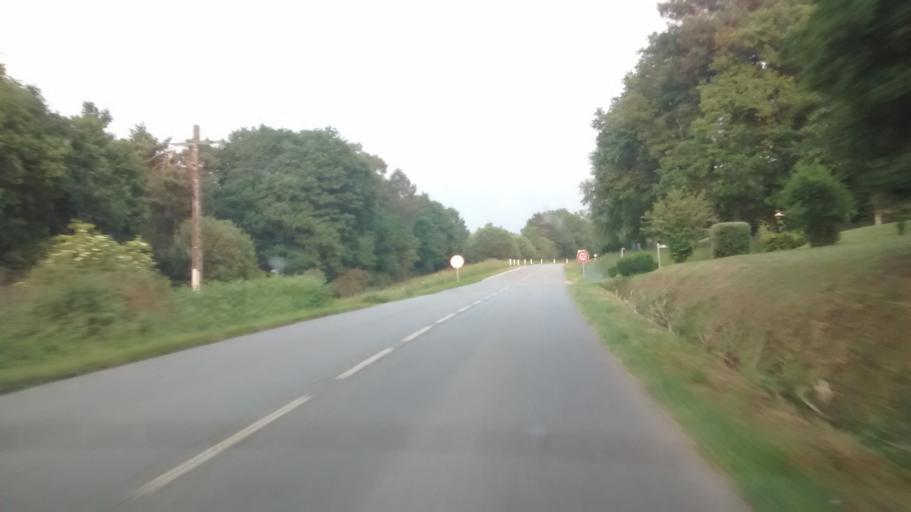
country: FR
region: Brittany
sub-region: Departement du Morbihan
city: Beignon
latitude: 47.9532
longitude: -2.1393
